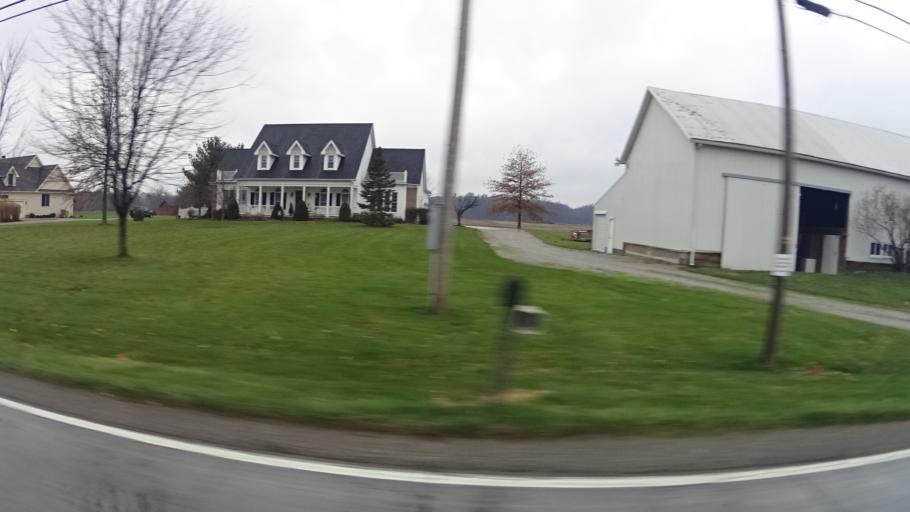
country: US
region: Ohio
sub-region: Lorain County
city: Lagrange
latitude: 41.2669
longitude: -82.1388
